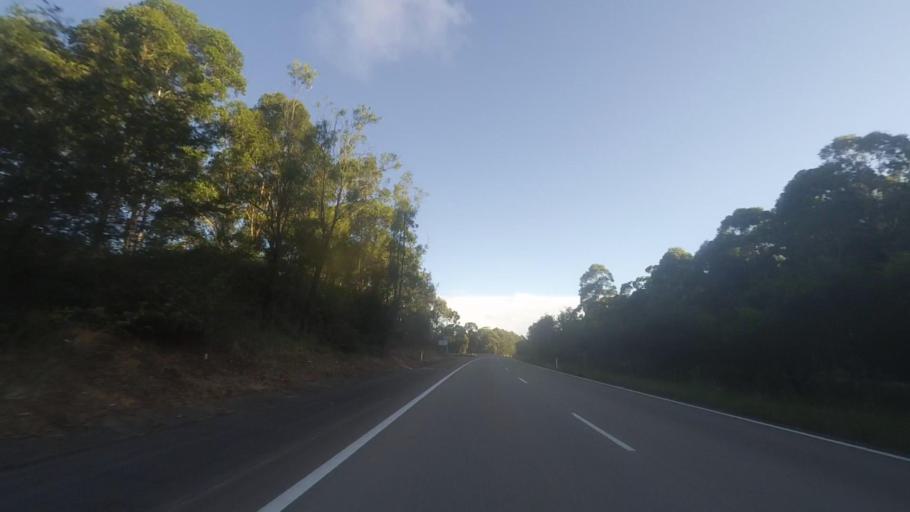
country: AU
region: New South Wales
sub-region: Great Lakes
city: Bulahdelah
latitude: -32.2975
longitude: 152.3455
